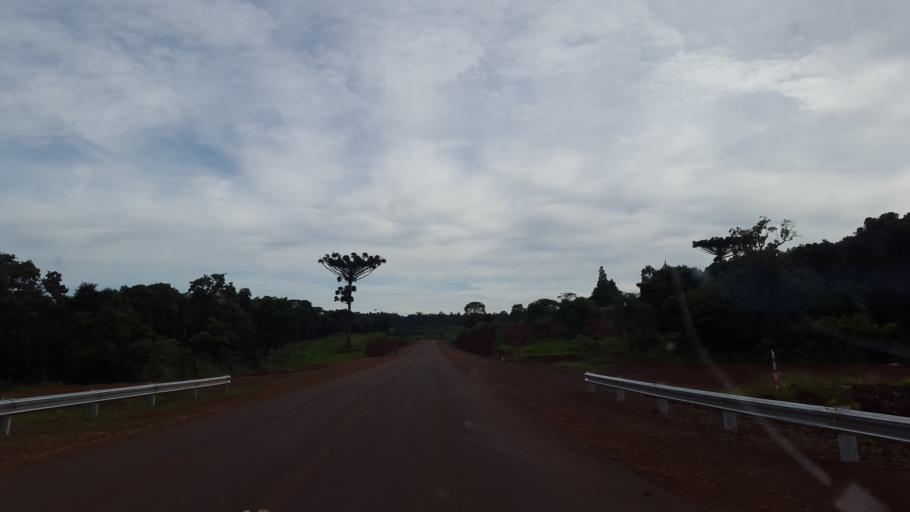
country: AR
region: Misiones
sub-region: Departamento de San Pedro
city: San Pedro
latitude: -26.4636
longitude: -53.8751
